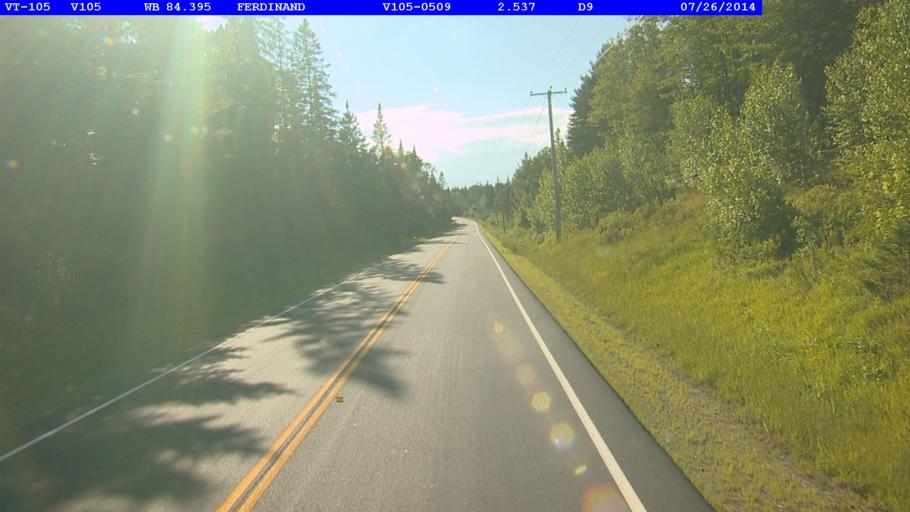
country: US
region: New Hampshire
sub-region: Coos County
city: Stratford
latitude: 44.7788
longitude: -71.7546
